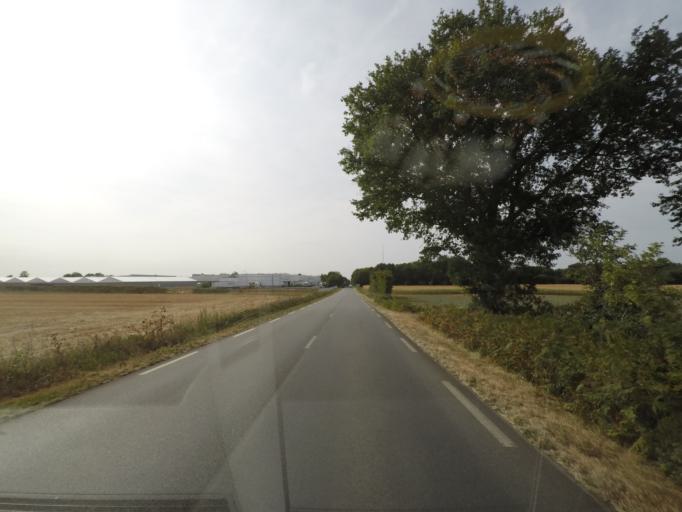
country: FR
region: Poitou-Charentes
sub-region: Departement des Deux-Sevres
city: Lezay
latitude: 46.1795
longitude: -0.0219
